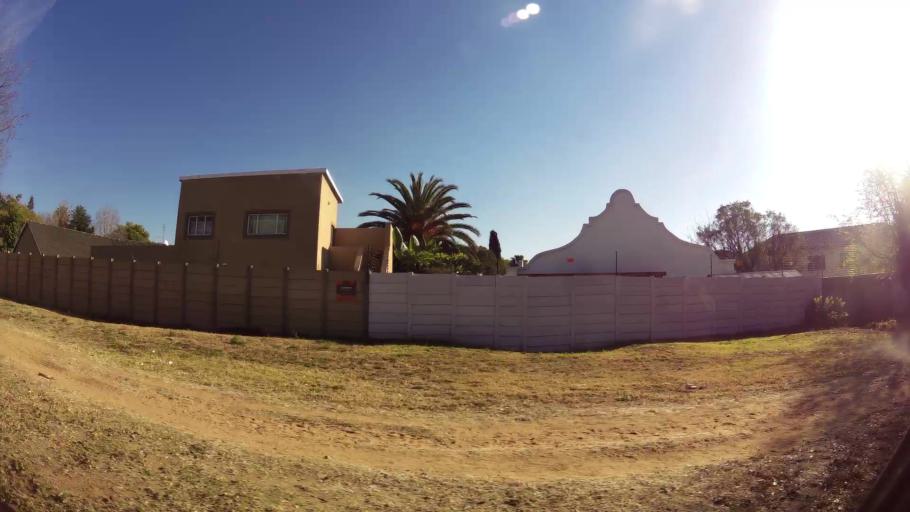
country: ZA
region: Gauteng
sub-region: City of Johannesburg Metropolitan Municipality
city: Diepsloot
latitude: -26.0529
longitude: 27.9777
